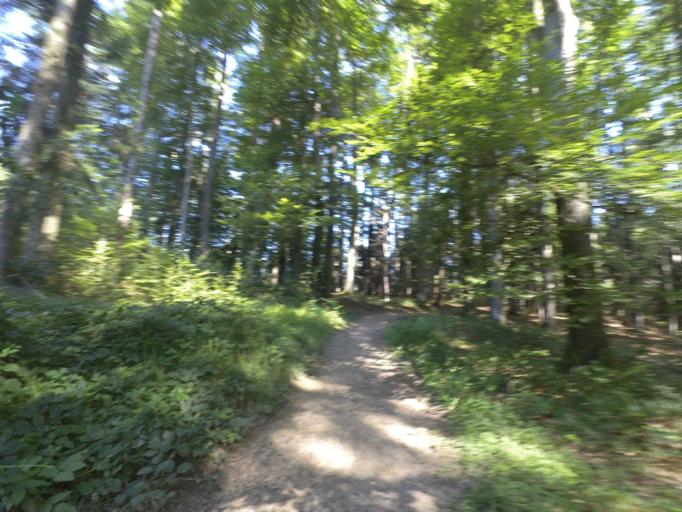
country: AT
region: Salzburg
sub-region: Politischer Bezirk Salzburg-Umgebung
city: Mattsee
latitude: 47.9594
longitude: 13.1137
